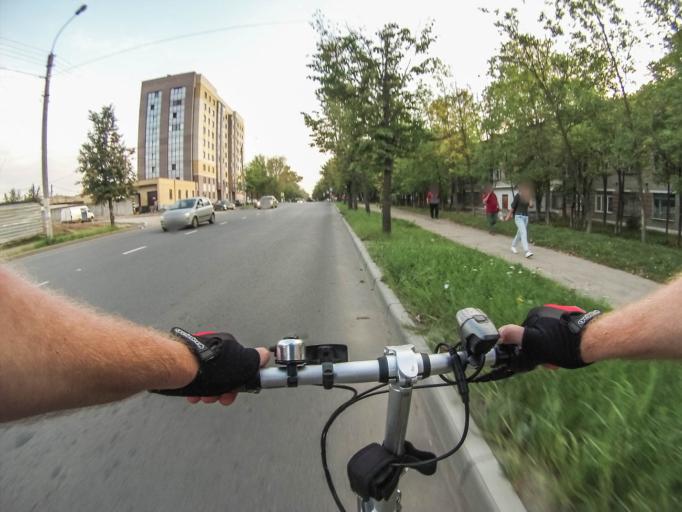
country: RU
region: Kostroma
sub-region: Kostromskoy Rayon
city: Kostroma
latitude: 57.7931
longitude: 40.9471
